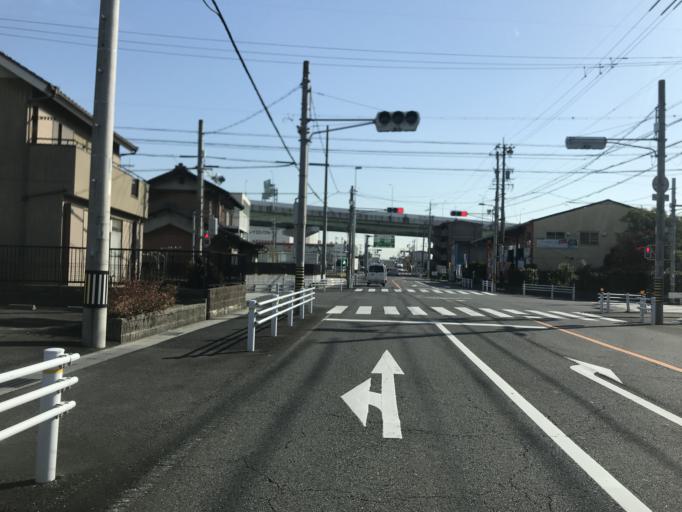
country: JP
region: Aichi
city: Iwakura
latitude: 35.2302
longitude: 136.8497
